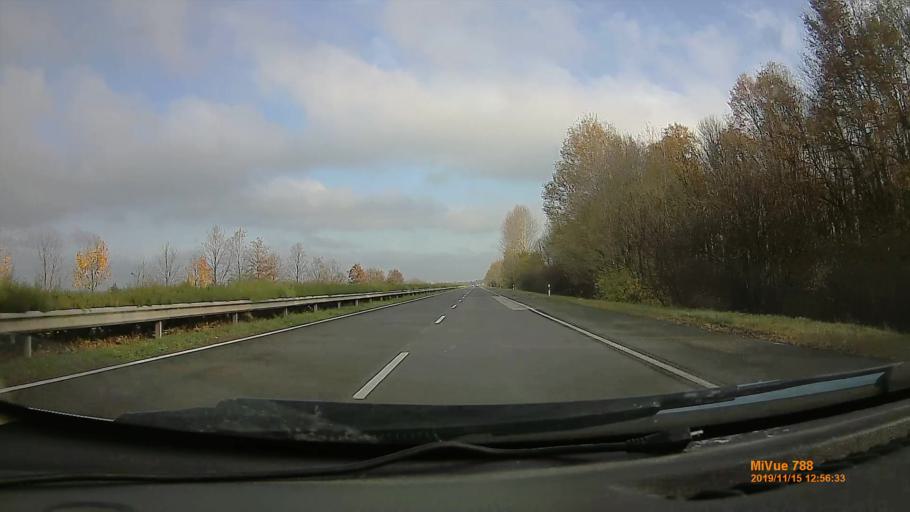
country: HU
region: Bekes
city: Bekescsaba
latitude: 46.6747
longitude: 21.1455
